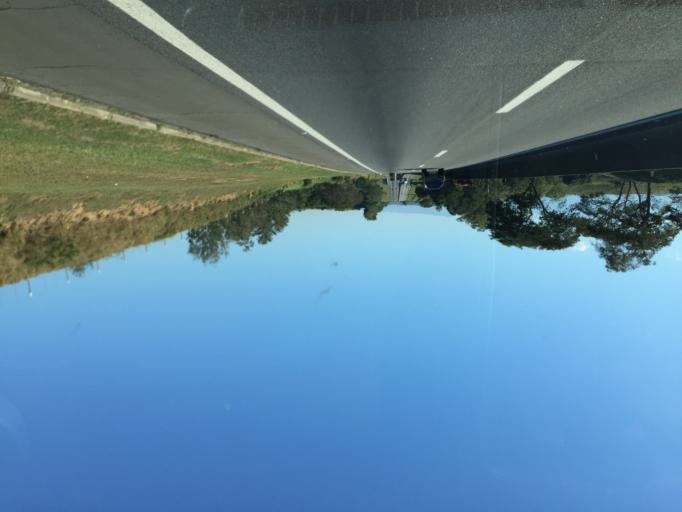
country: BR
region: Sao Paulo
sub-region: Lorena
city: Lorena
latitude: -22.7002
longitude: -45.0341
